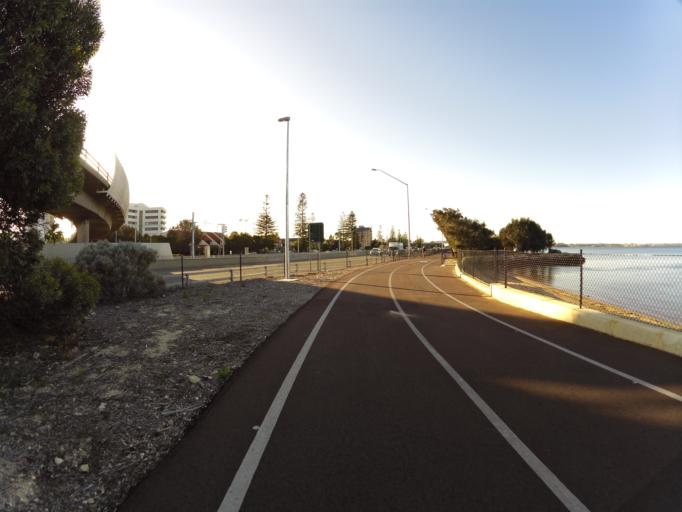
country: AU
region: Western Australia
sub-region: South Perth
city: South Perth
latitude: -31.9728
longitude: 115.8473
